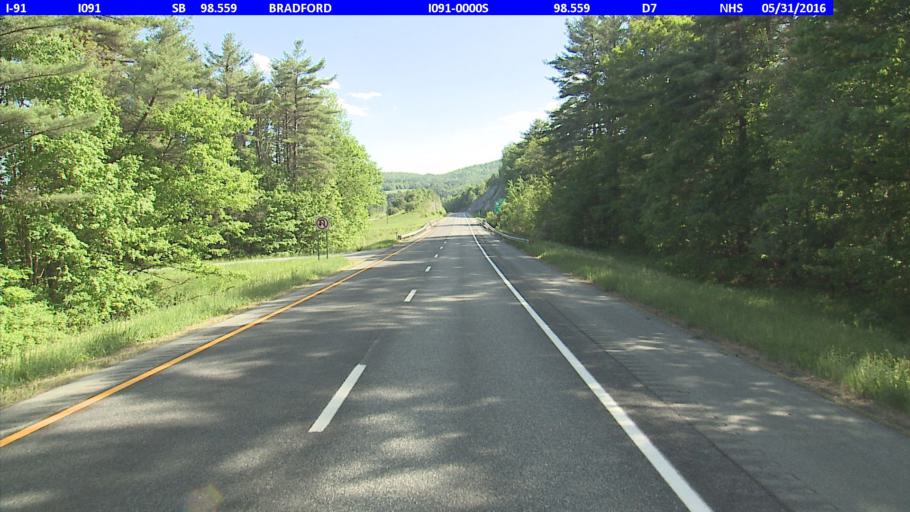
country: US
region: New Hampshire
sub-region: Grafton County
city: Haverhill
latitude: 43.9956
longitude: -72.1329
